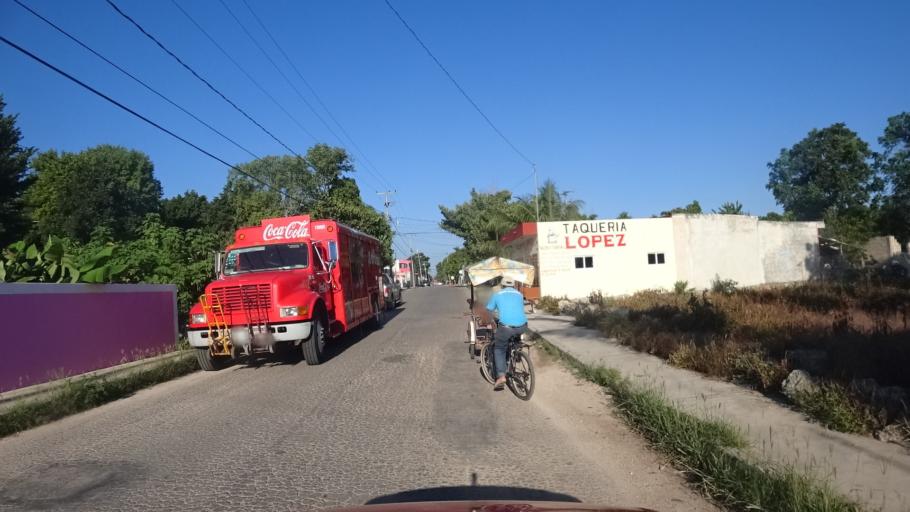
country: MX
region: Yucatan
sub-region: Tizimin
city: Tizimin
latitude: 21.1541
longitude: -88.1554
